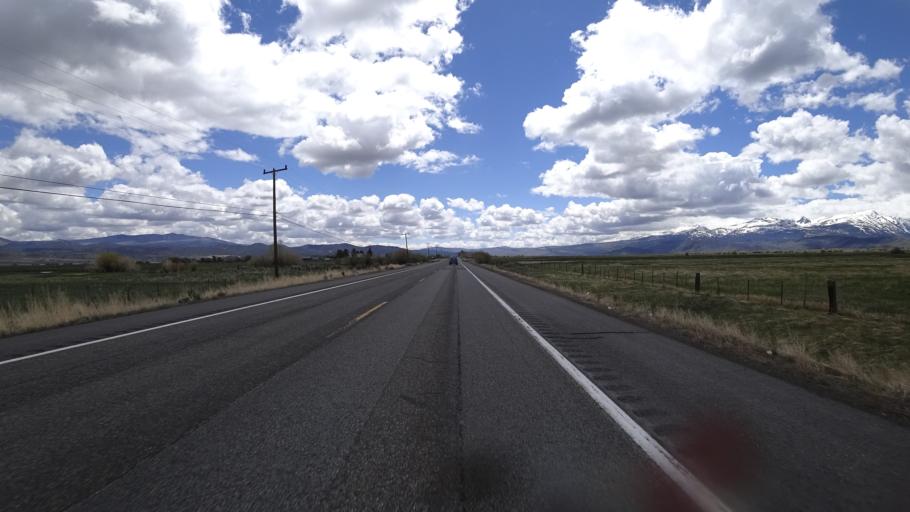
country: US
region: California
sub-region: Mono County
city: Bridgeport
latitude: 38.2651
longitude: -119.2786
